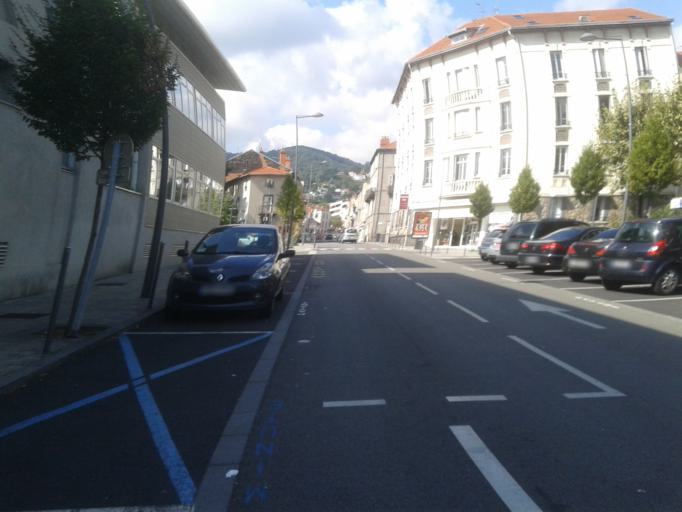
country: FR
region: Auvergne
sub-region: Departement du Puy-de-Dome
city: Chamalieres
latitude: 45.7776
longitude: 3.0669
